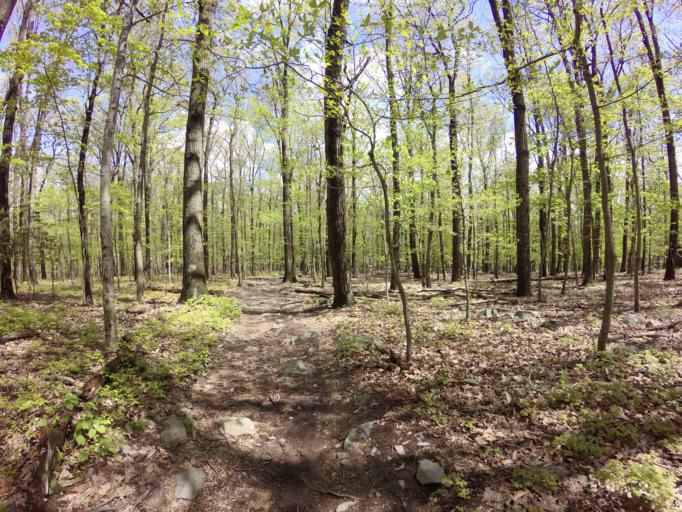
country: US
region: Maryland
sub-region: Washington County
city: Boonsboro
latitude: 39.5325
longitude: -77.6091
